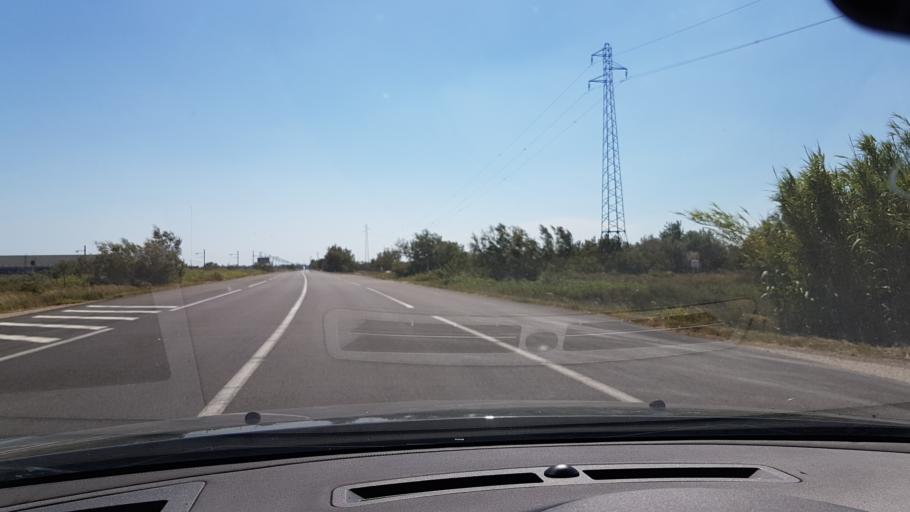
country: FR
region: Provence-Alpes-Cote d'Azur
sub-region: Departement des Bouches-du-Rhone
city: Port-Saint-Louis-du-Rhone
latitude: 43.4214
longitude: 4.8114
